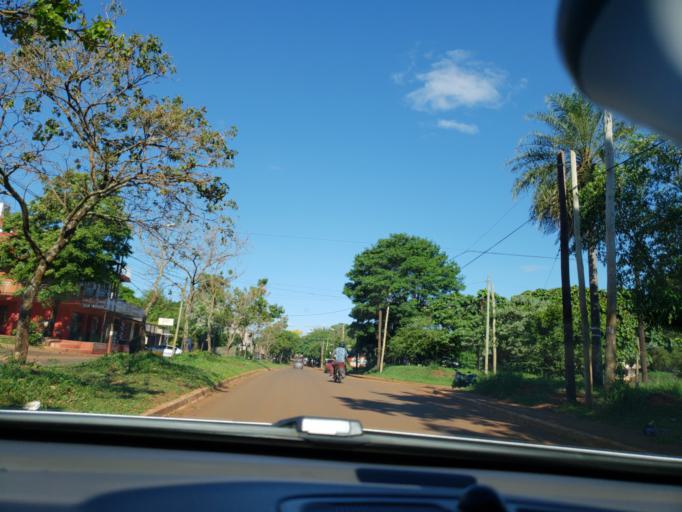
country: AR
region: Misiones
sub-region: Departamento de Capital
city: Posadas
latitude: -27.3836
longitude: -55.9372
